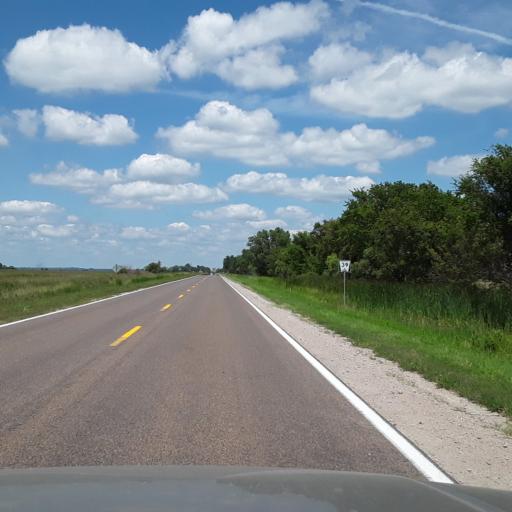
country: US
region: Nebraska
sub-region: Nance County
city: Genoa
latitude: 41.3524
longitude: -97.6950
